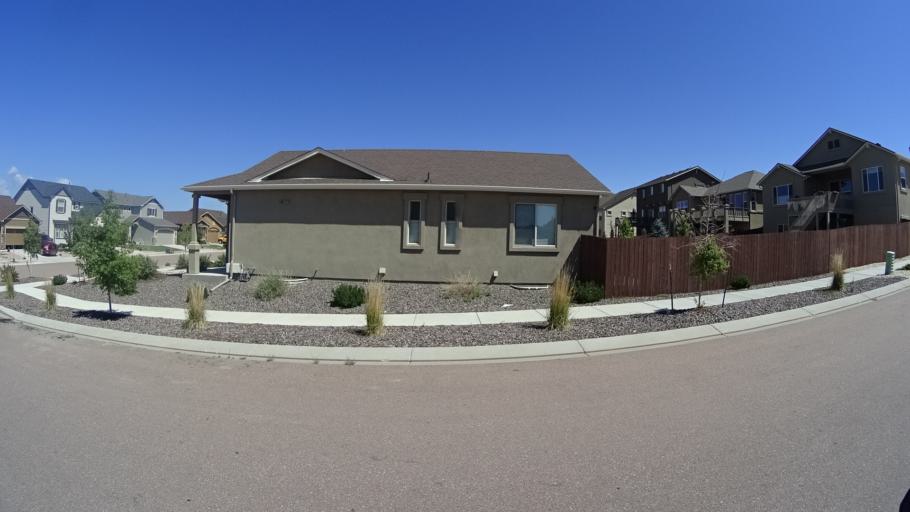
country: US
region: Colorado
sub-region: El Paso County
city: Black Forest
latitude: 38.9877
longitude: -104.7594
